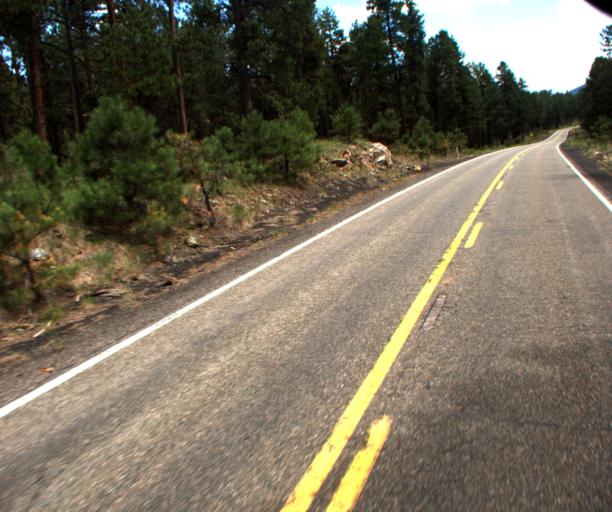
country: US
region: Arizona
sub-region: Coconino County
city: Flagstaff
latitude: 35.3035
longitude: -111.7684
